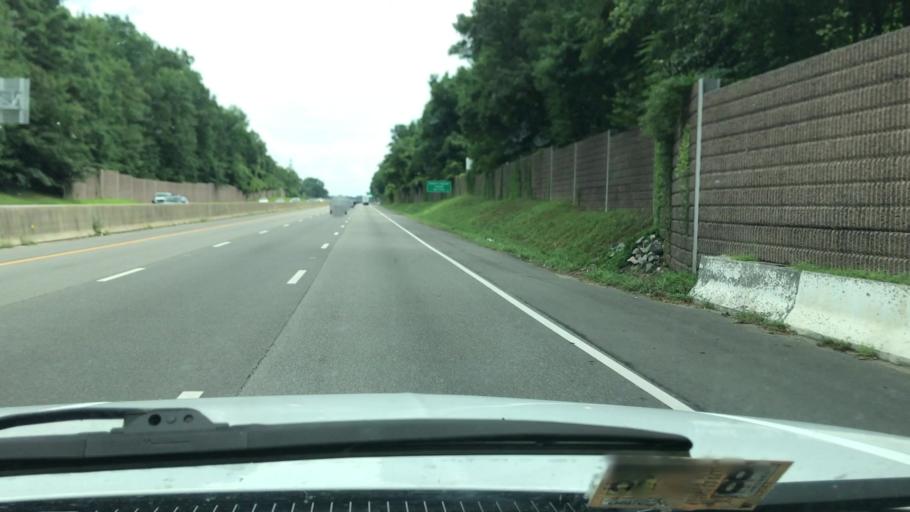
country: US
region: Virginia
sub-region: Chesterfield County
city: Bon Air
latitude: 37.4881
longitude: -77.5194
